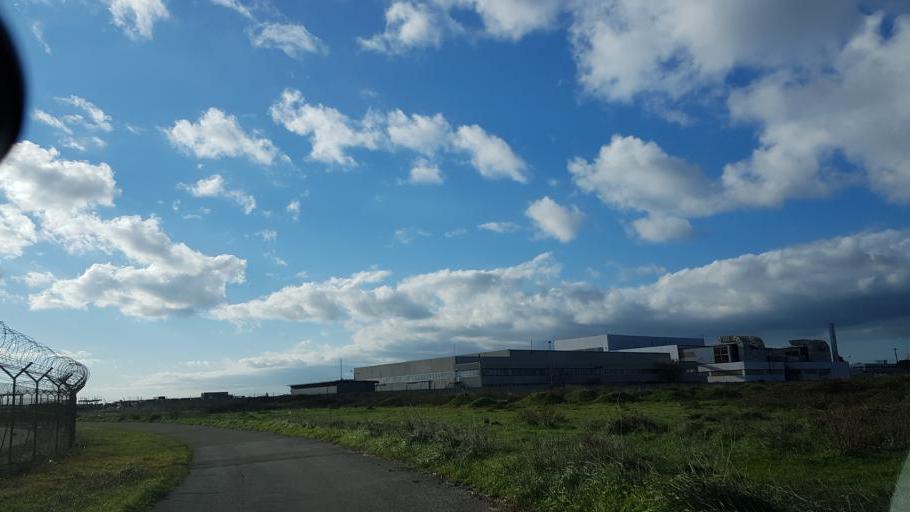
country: IT
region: Apulia
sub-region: Provincia di Brindisi
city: Materdomini
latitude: 40.6759
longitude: 17.9222
